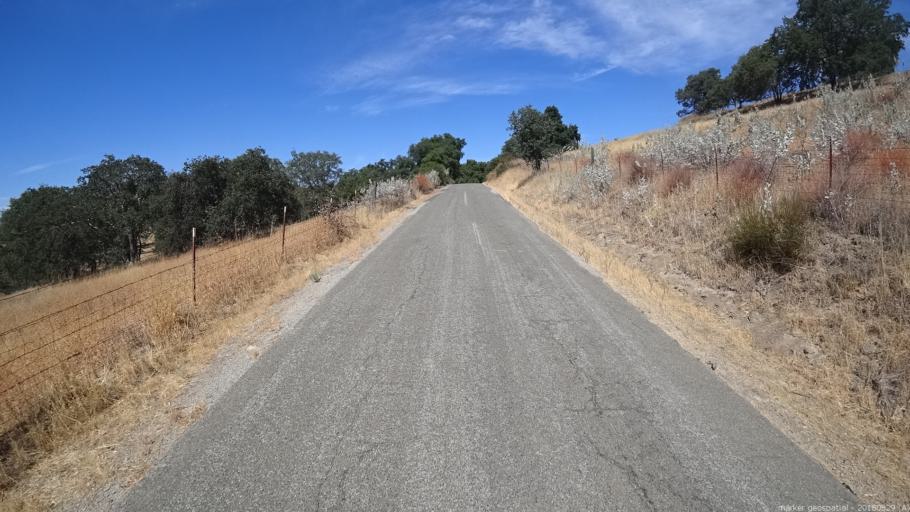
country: US
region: California
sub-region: San Luis Obispo County
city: Lake Nacimiento
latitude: 35.8066
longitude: -121.0377
